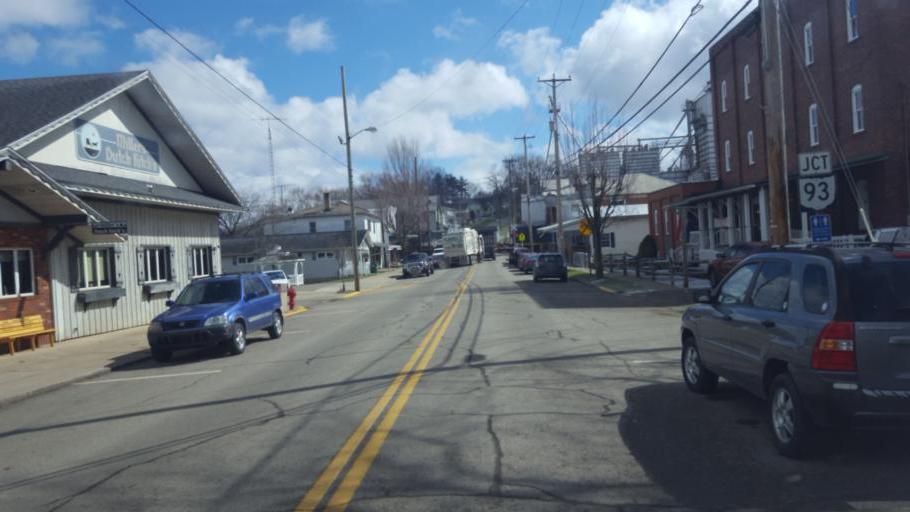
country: US
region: Ohio
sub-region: Tuscarawas County
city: Sugarcreek
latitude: 40.4404
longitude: -81.7039
